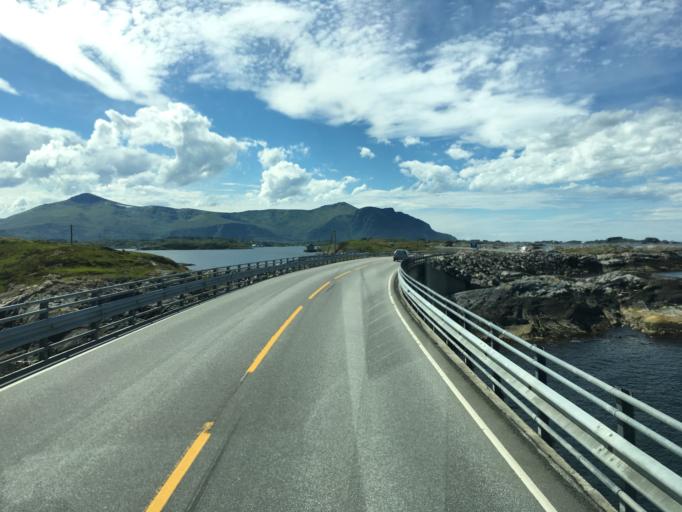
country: NO
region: More og Romsdal
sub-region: Eide
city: Eide
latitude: 63.0156
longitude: 7.3421
